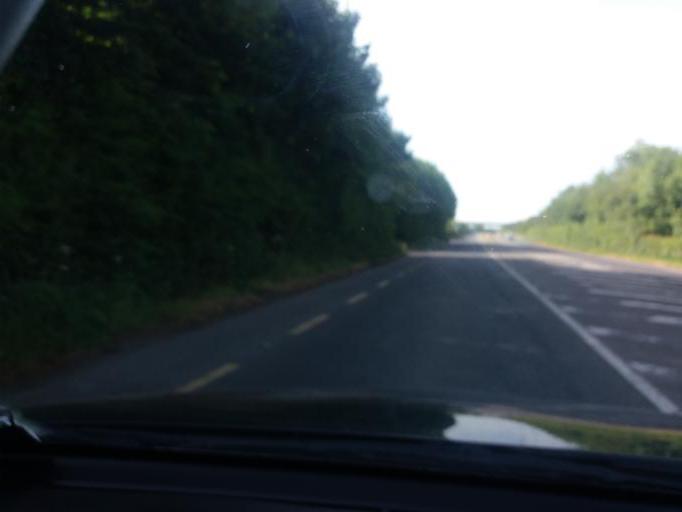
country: IE
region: Leinster
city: Balrothery
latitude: 53.5474
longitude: -6.2068
